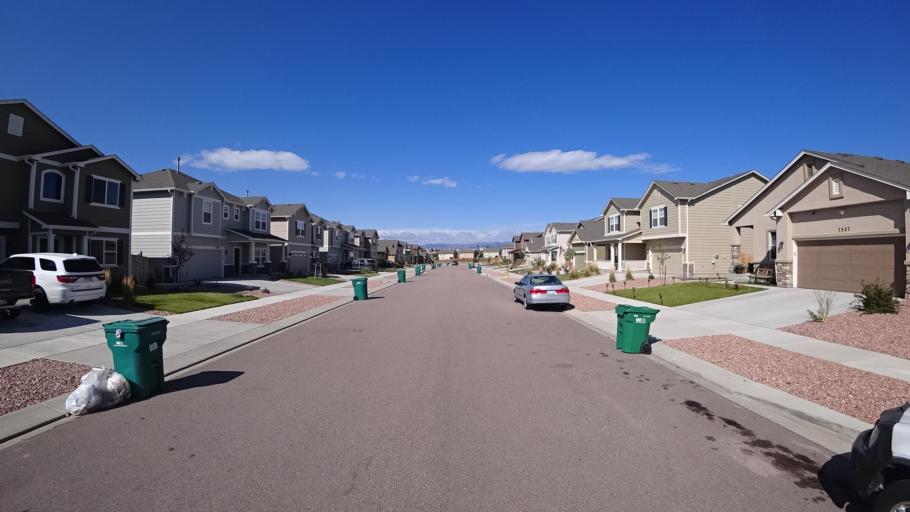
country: US
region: Colorado
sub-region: El Paso County
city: Cimarron Hills
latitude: 38.9304
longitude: -104.6929
